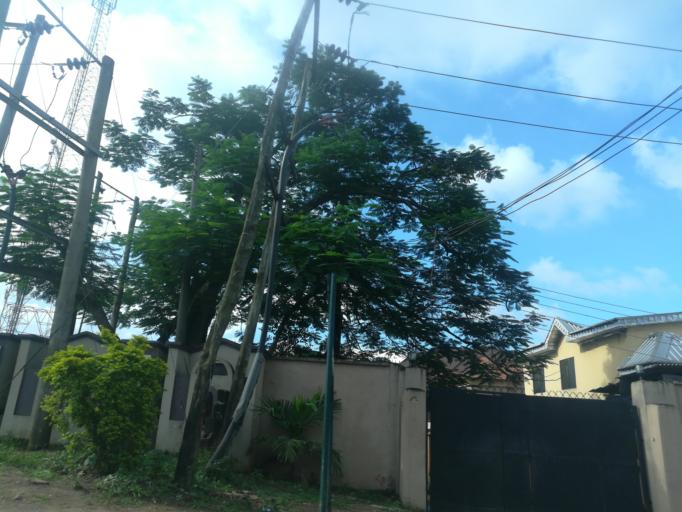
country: NG
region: Lagos
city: Ikeja
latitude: 6.6185
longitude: 3.3629
